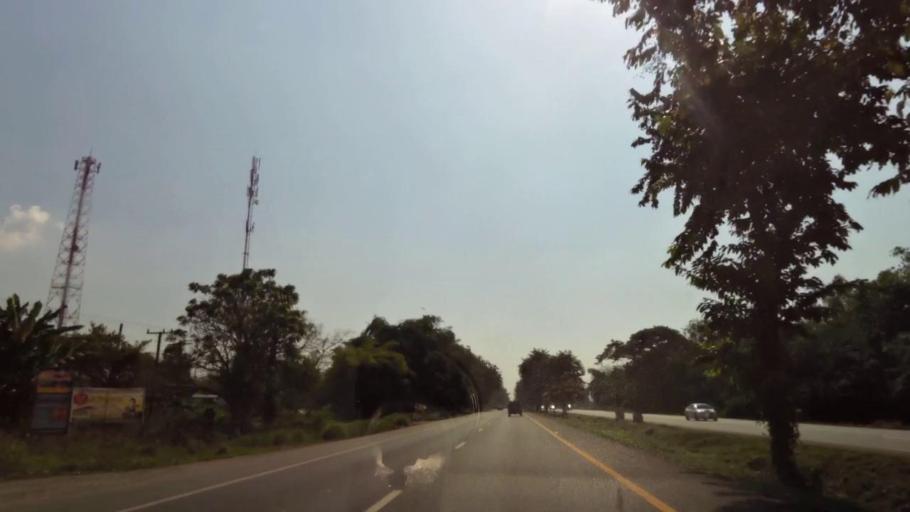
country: TH
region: Phichit
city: Bueng Na Rang
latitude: 16.0953
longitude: 100.1254
